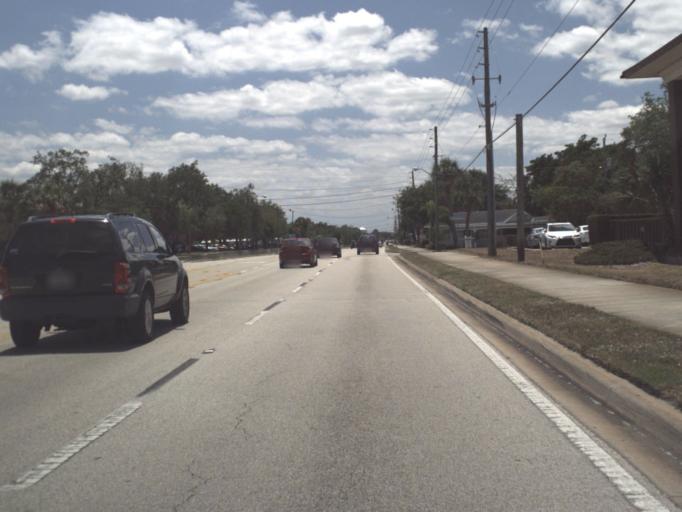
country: US
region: Florida
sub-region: Brevard County
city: Melbourne
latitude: 28.0758
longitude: -80.6215
